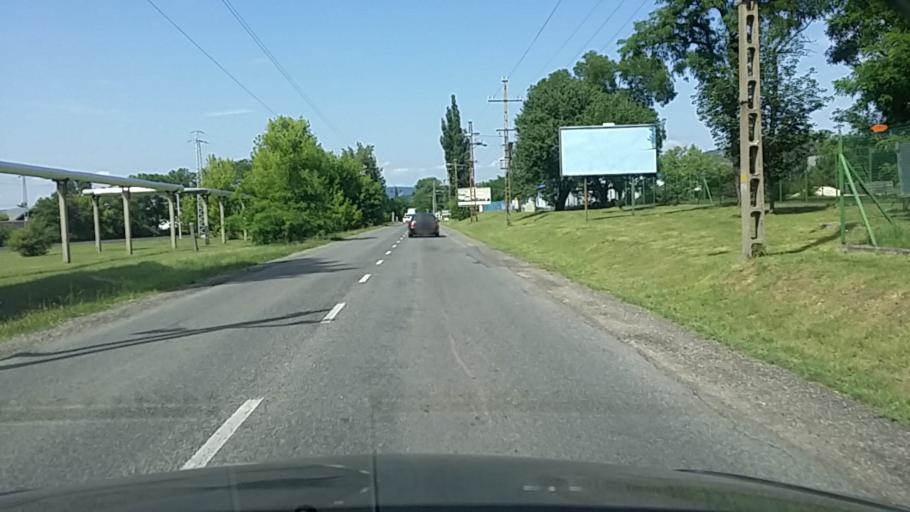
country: HU
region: Komarom-Esztergom
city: Dorog
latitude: 47.7512
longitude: 18.7319
